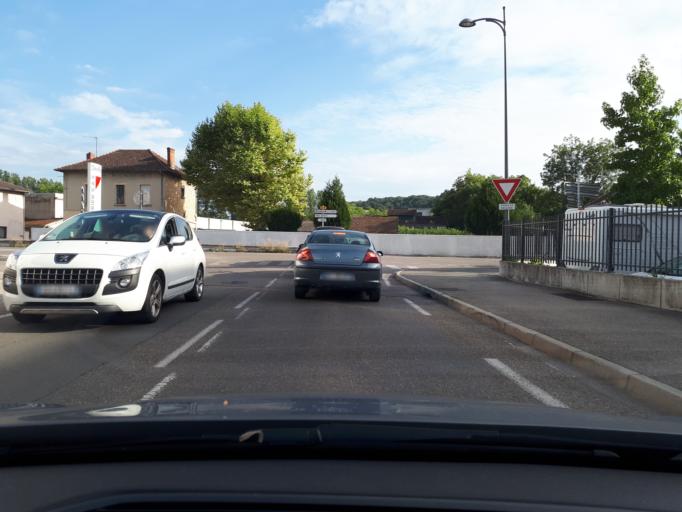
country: FR
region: Rhone-Alpes
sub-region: Departement de l'Isere
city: Bourgoin
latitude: 45.5885
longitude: 5.2965
